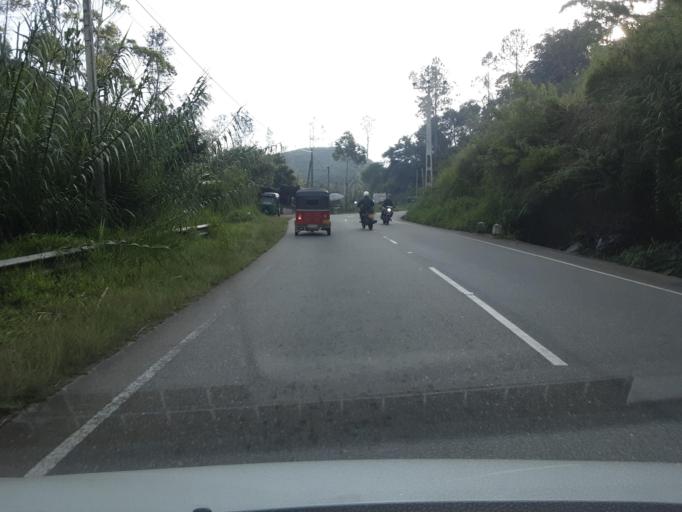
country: LK
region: Uva
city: Badulla
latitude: 6.9308
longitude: 80.9793
